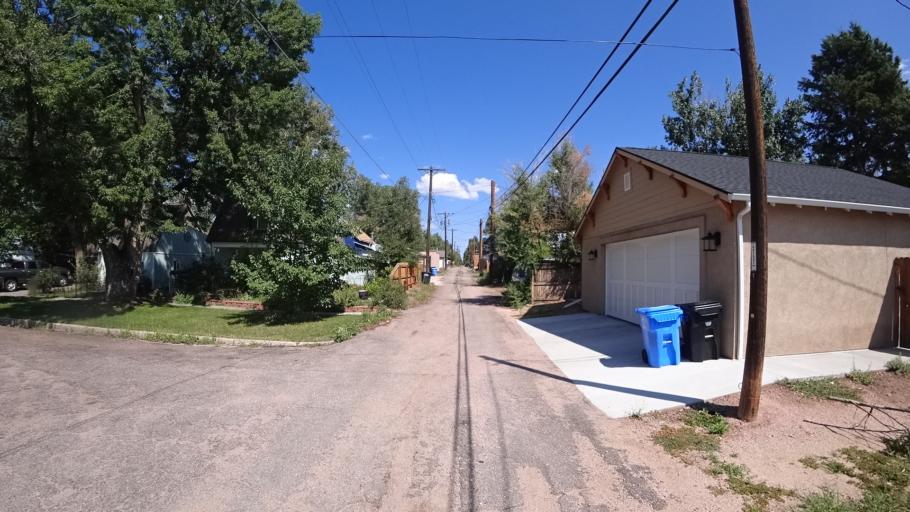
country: US
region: Colorado
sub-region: El Paso County
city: Colorado Springs
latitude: 38.8548
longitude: -104.8145
